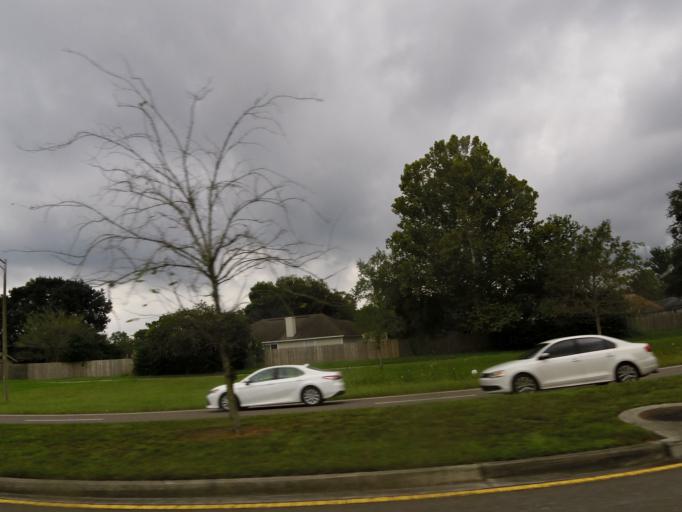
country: US
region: Florida
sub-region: Clay County
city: Bellair-Meadowbrook Terrace
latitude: 30.1992
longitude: -81.7984
